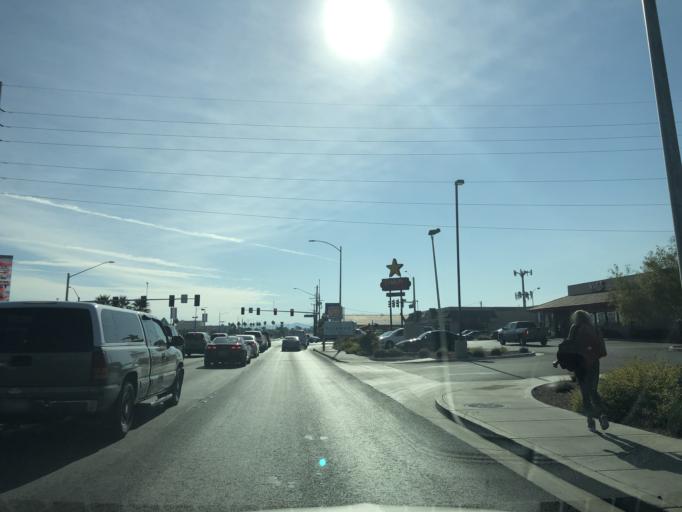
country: US
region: Nevada
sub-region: Clark County
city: Winchester
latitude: 36.1306
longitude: -115.1371
